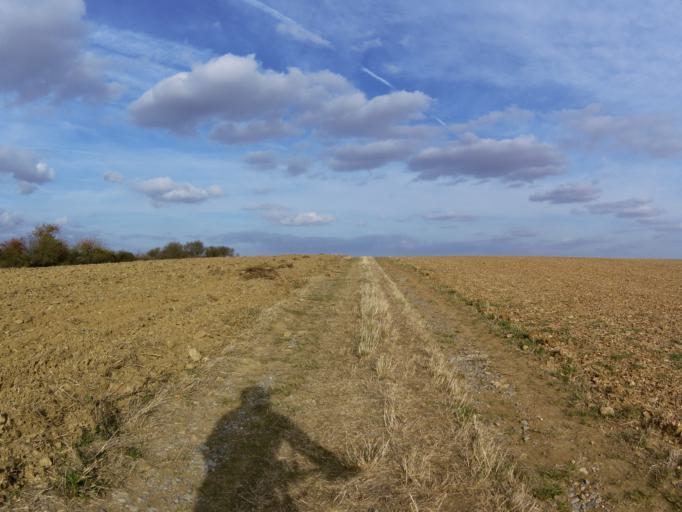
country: DE
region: Bavaria
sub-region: Regierungsbezirk Unterfranken
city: Reichenberg
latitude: 49.7281
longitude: 9.9418
